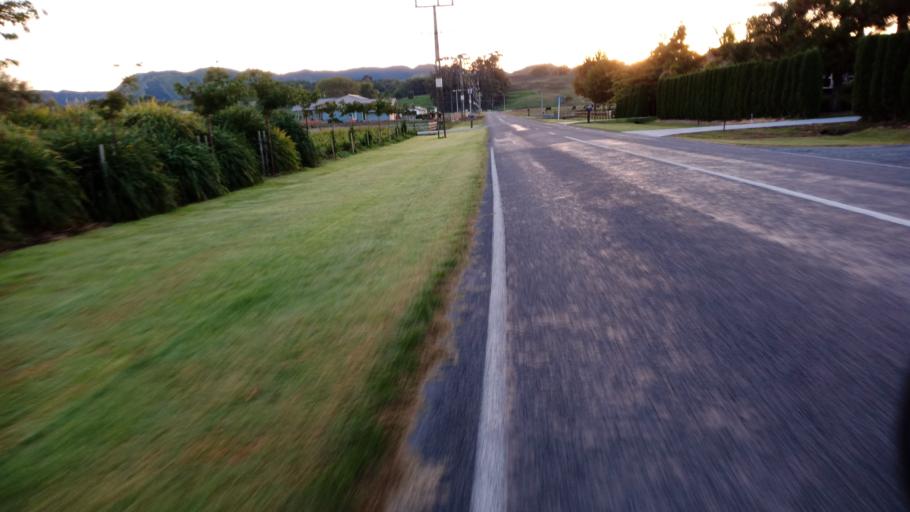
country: NZ
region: Gisborne
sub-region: Gisborne District
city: Gisborne
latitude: -38.6334
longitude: 177.9874
